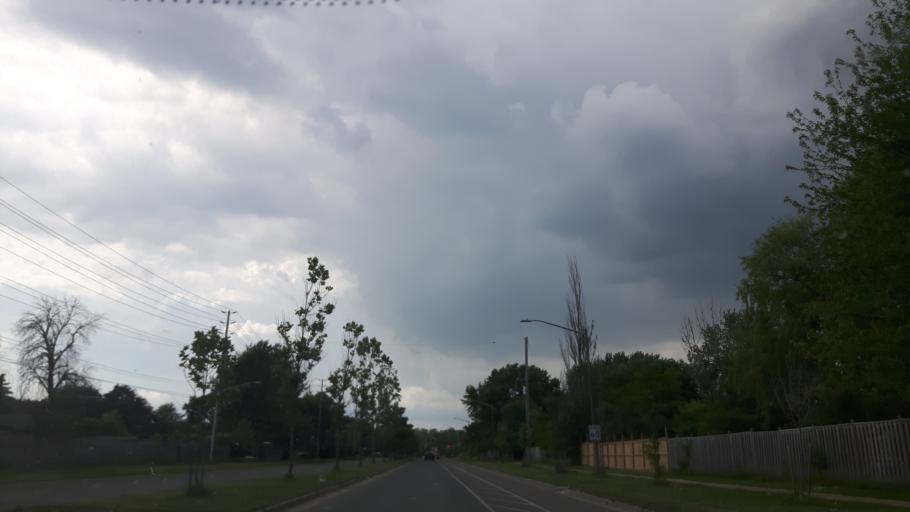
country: CA
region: Ontario
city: London
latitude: 42.9394
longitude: -81.2104
